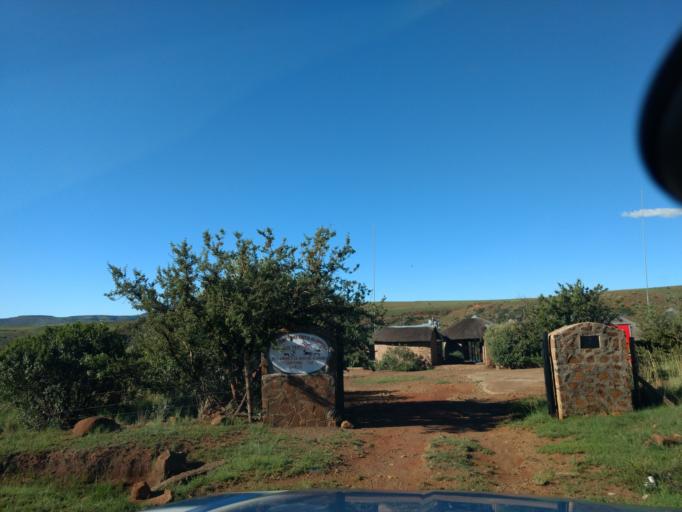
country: LS
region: Berea
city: Teyateyaneng
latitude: -29.3632
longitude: 27.7873
